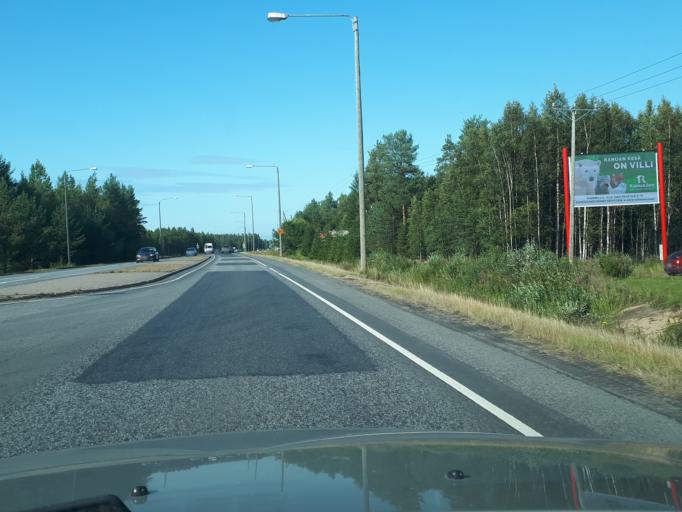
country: FI
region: Northern Ostrobothnia
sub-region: Oulunkaari
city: Ii
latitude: 65.2913
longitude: 25.3733
